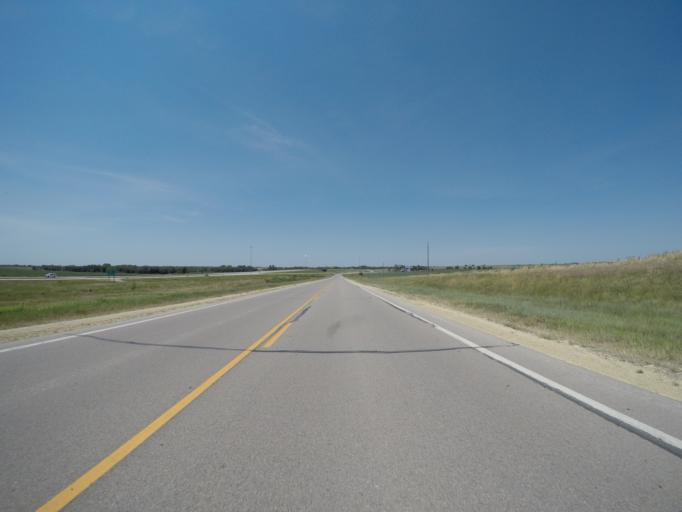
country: US
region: Kansas
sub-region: Ottawa County
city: Minneapolis
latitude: 39.1128
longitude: -97.6602
